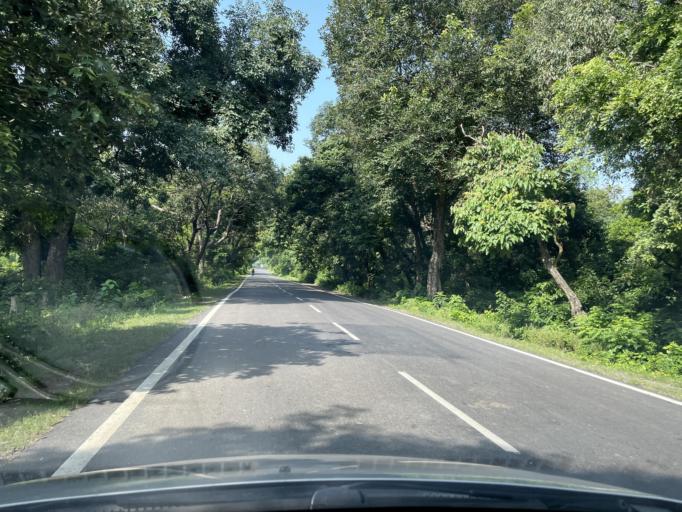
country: IN
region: Uttarakhand
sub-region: Naini Tal
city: Kaladhungi
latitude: 29.2186
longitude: 79.2309
